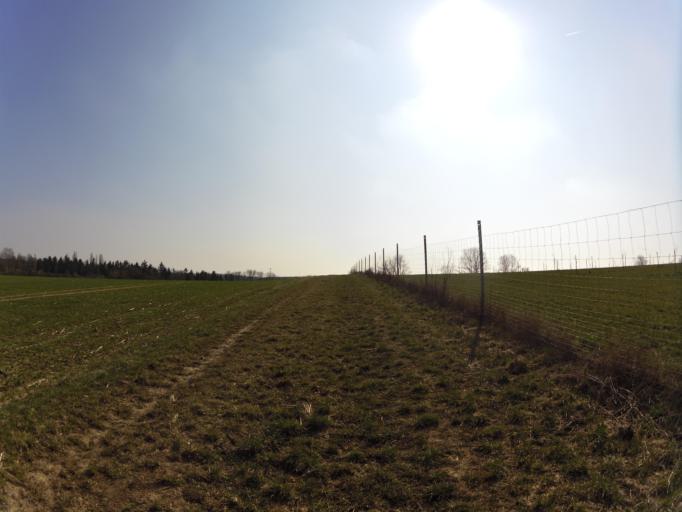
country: DE
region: Bavaria
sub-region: Regierungsbezirk Unterfranken
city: Winterhausen
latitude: 49.6748
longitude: 9.9882
